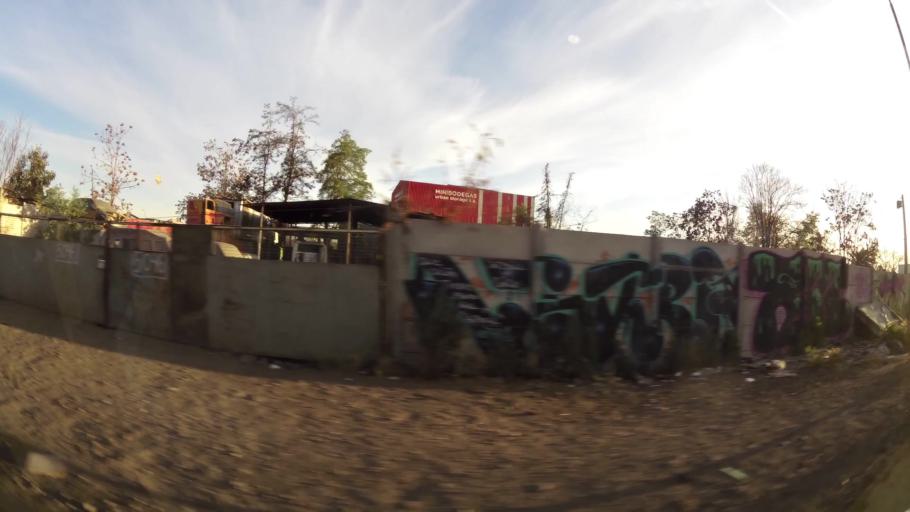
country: CL
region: Santiago Metropolitan
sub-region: Provincia de Santiago
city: Lo Prado
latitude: -33.4088
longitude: -70.7049
